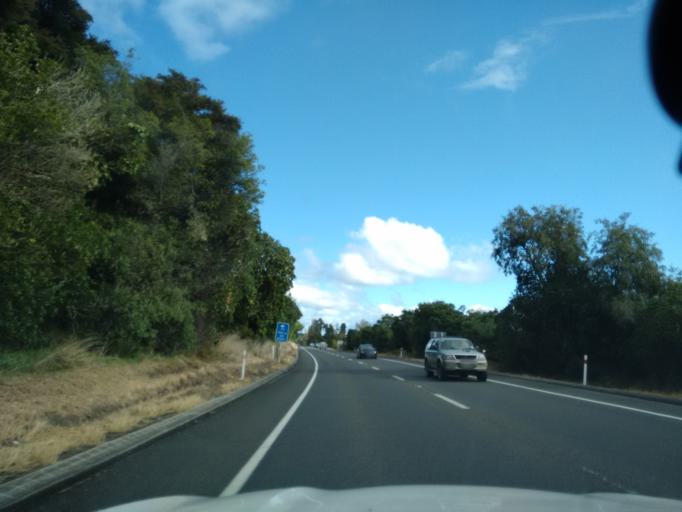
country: NZ
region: Waikato
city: Turangi
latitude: -38.8886
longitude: 175.9520
